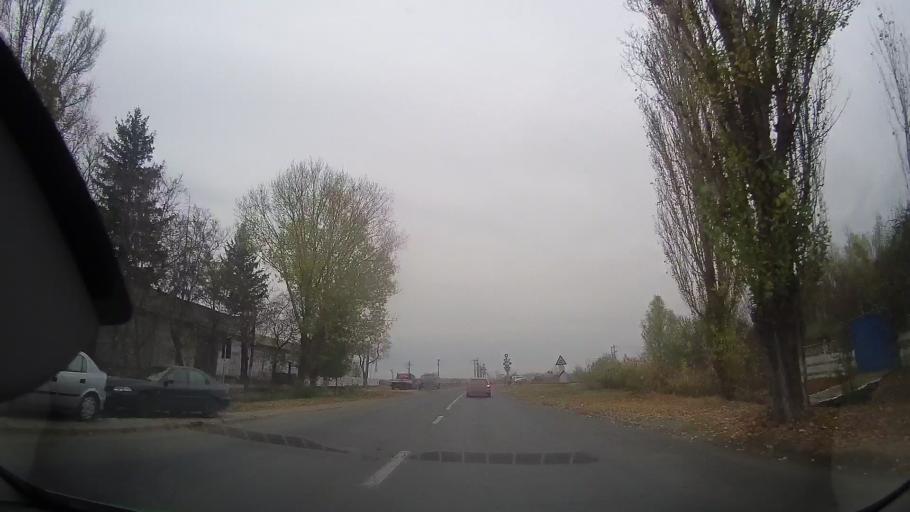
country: RO
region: Ialomita
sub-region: Comuna Slobozia
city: Slobozia
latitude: 44.5790
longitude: 27.3382
